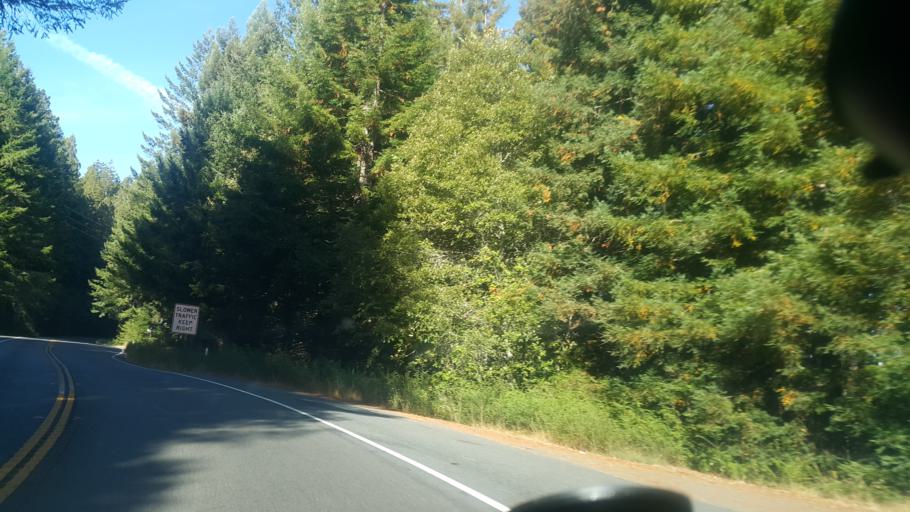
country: US
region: California
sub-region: Mendocino County
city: Fort Bragg
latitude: 39.3654
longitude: -123.6732
